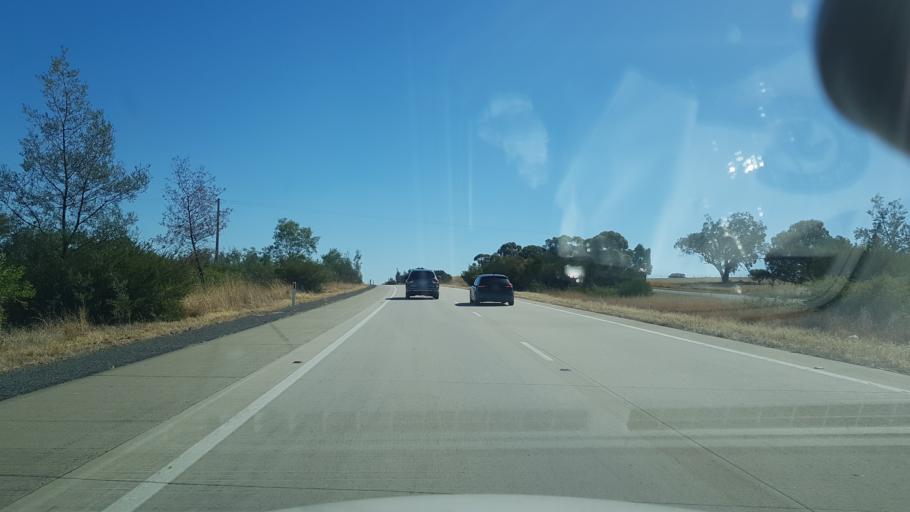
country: AU
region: New South Wales
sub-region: Greater Hume Shire
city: Jindera
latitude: -35.9244
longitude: 147.0560
